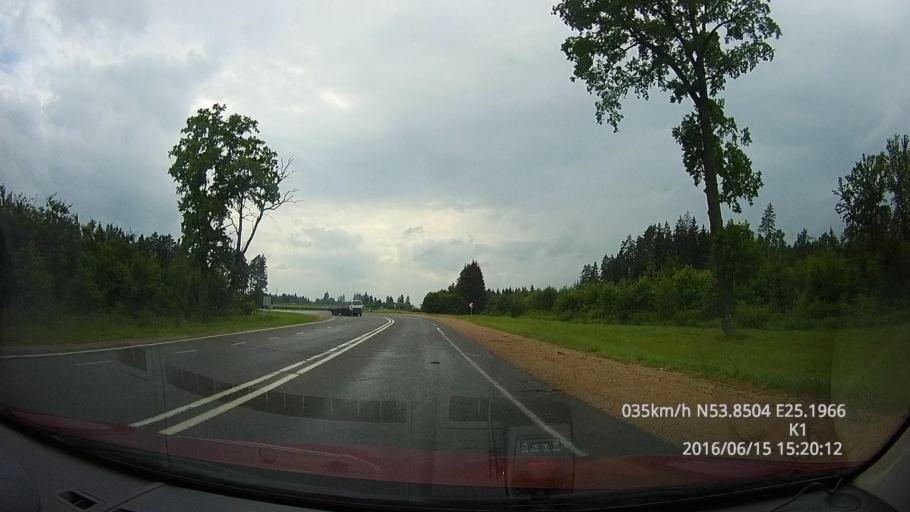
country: BY
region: Grodnenskaya
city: Lida
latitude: 53.8501
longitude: 25.1963
